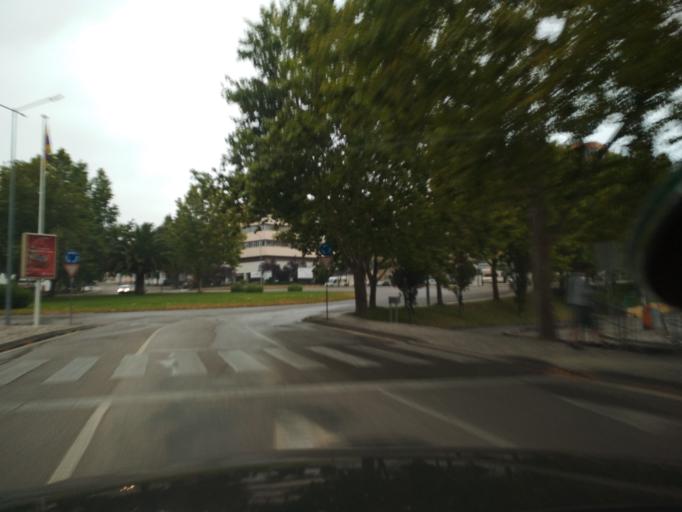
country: PT
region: Coimbra
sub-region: Coimbra
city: Coimbra
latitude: 40.1946
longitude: -8.4070
